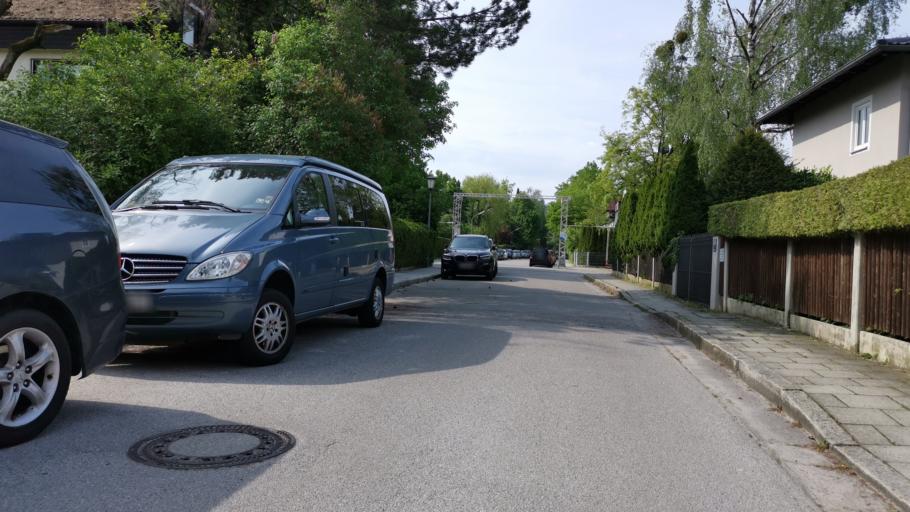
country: DE
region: Bavaria
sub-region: Upper Bavaria
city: Pullach im Isartal
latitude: 48.0861
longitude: 11.5215
